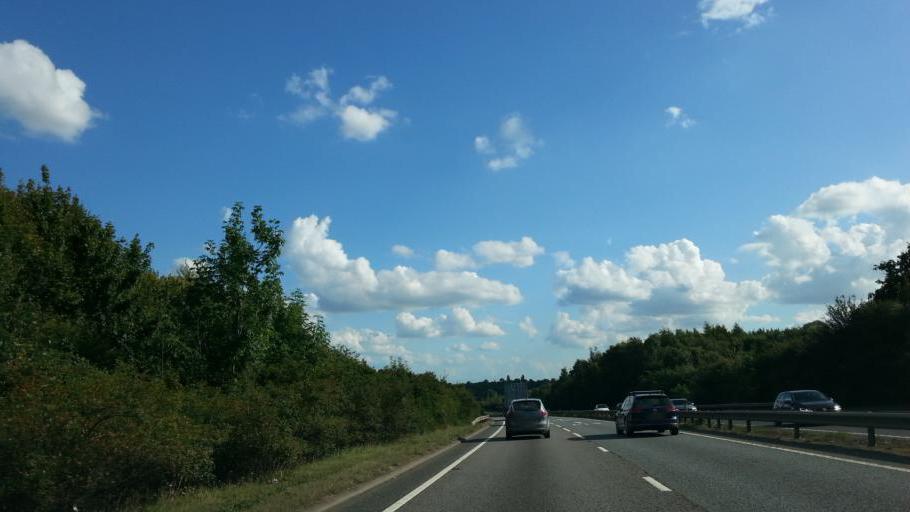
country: GB
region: England
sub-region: Suffolk
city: Bramford
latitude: 52.0416
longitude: 1.0954
